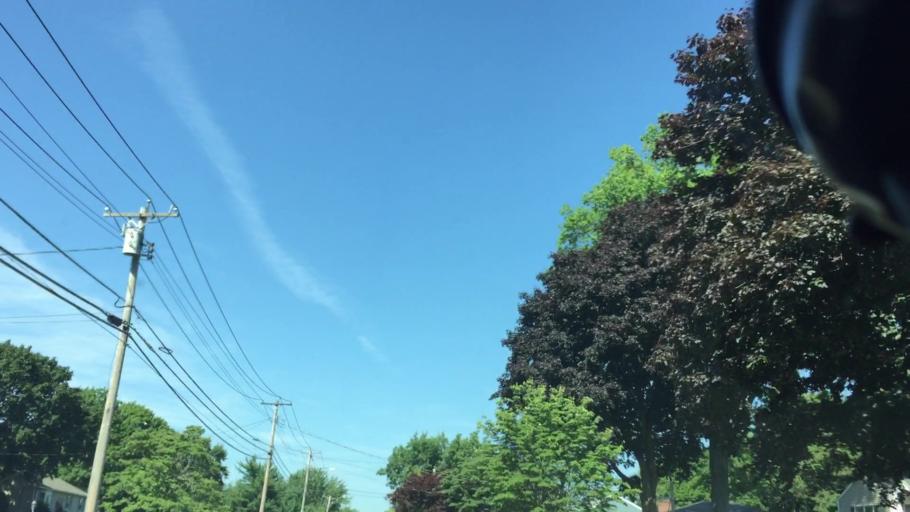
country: US
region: Connecticut
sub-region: Fairfield County
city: Trumbull
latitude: 41.2412
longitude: -73.2085
